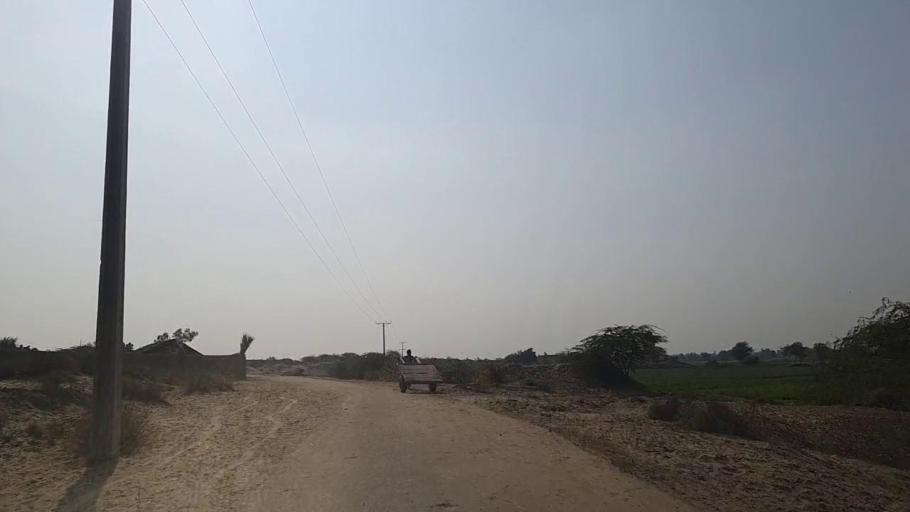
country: PK
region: Sindh
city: Daur
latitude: 26.4620
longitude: 68.4652
